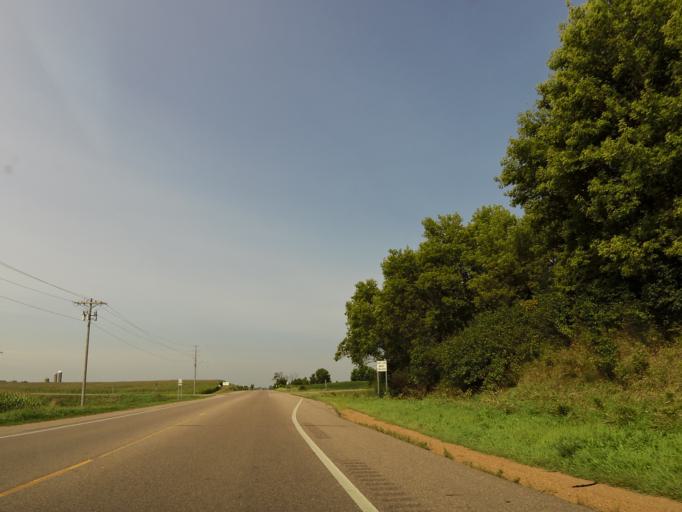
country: US
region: Minnesota
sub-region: Carver County
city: Cologne
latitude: 44.7671
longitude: -93.8267
